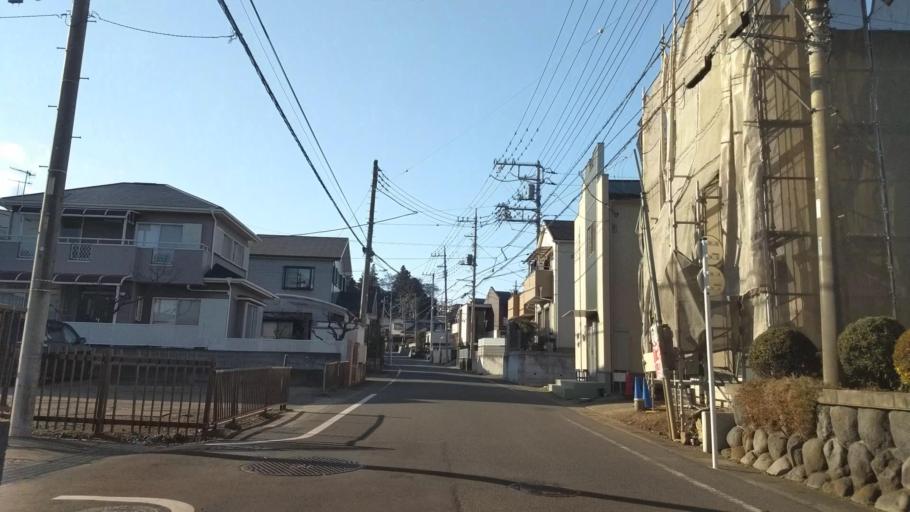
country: JP
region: Kanagawa
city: Hadano
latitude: 35.3613
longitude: 139.2674
